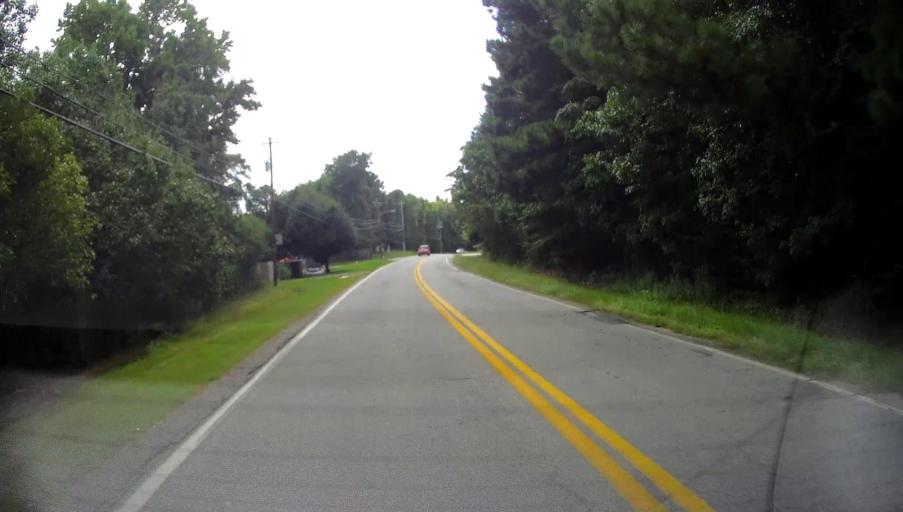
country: US
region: Alabama
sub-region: Russell County
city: Phenix City
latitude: 32.5644
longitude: -84.9530
